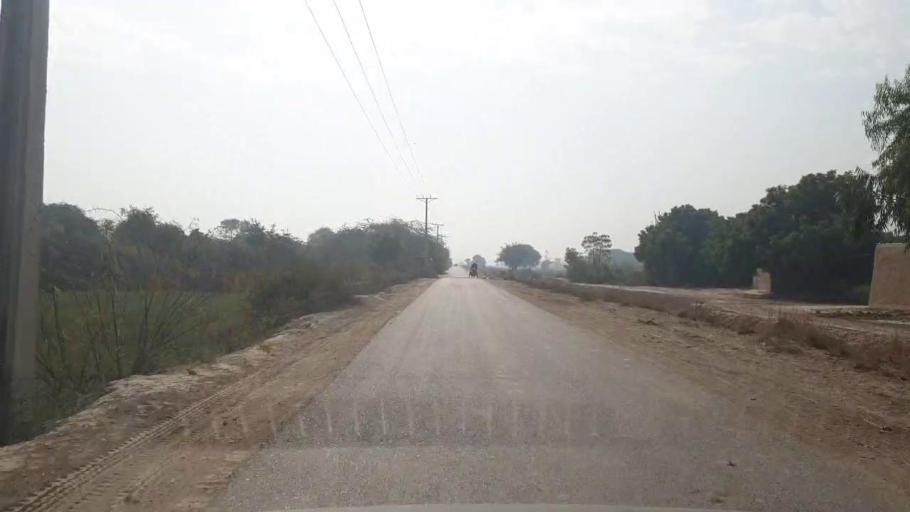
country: PK
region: Sindh
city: Hala
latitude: 25.7835
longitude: 68.4424
